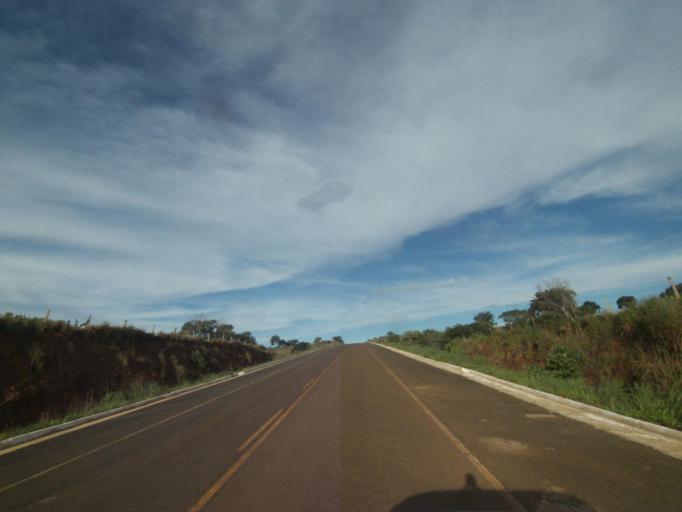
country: BR
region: Goias
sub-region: Jaragua
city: Jaragua
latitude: -15.8699
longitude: -49.4116
